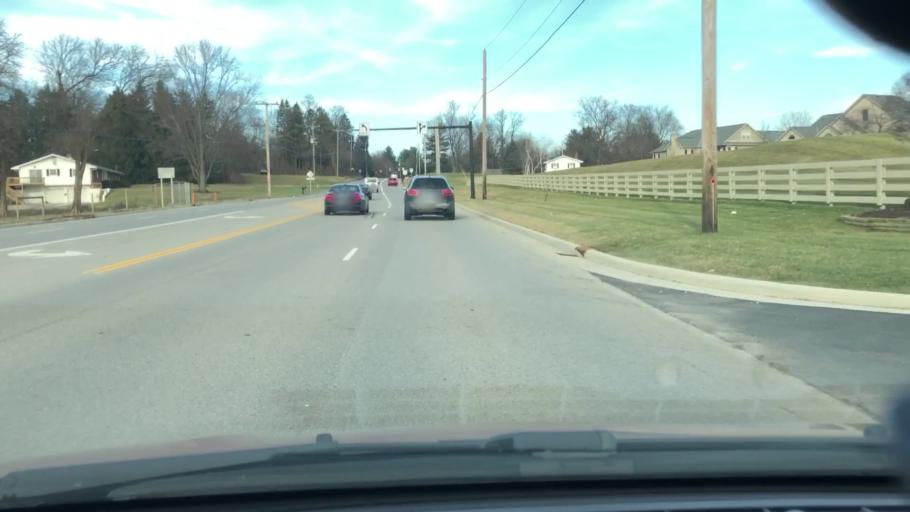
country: US
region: Ohio
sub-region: Franklin County
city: Westerville
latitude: 40.1536
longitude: -82.9496
